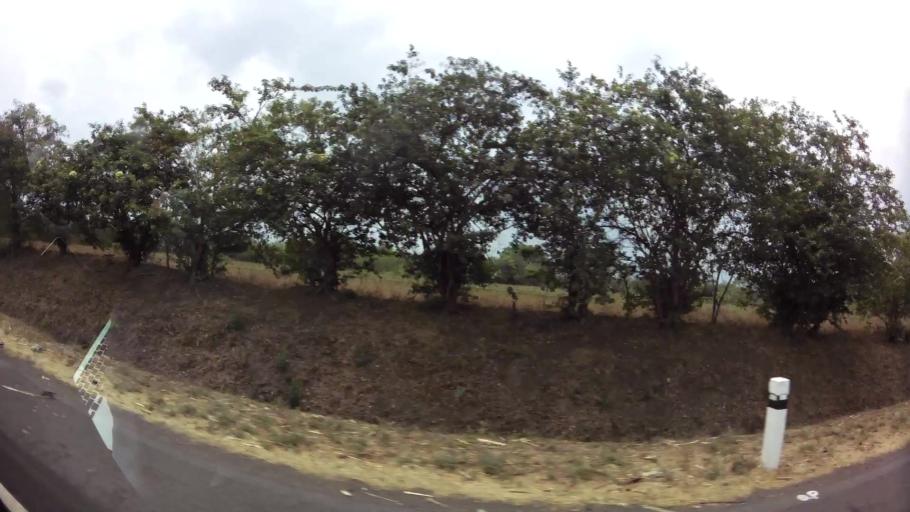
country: NI
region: Chinandega
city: Posoltega
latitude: 12.5493
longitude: -86.9316
